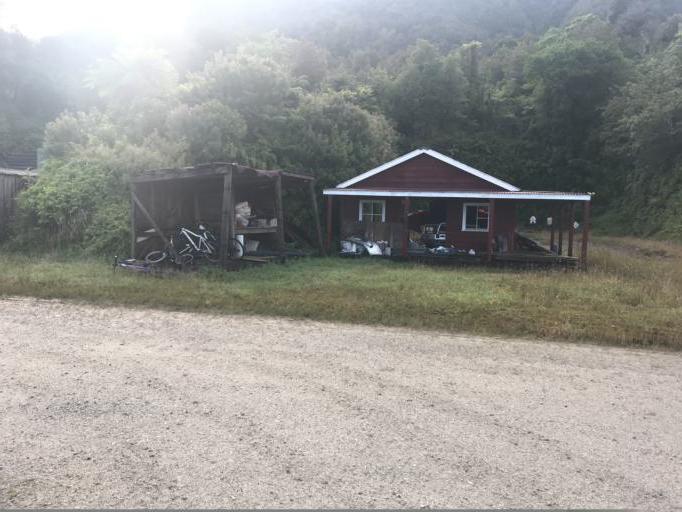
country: NZ
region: West Coast
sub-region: Westland District
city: Hokitika
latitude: -42.8239
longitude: 171.2502
